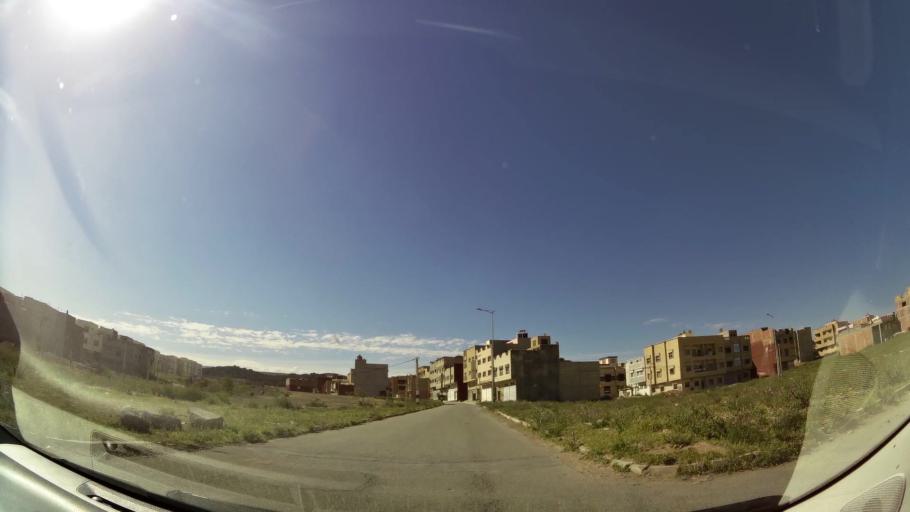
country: MA
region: Oriental
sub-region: Oujda-Angad
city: Oujda
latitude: 34.6541
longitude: -1.8838
